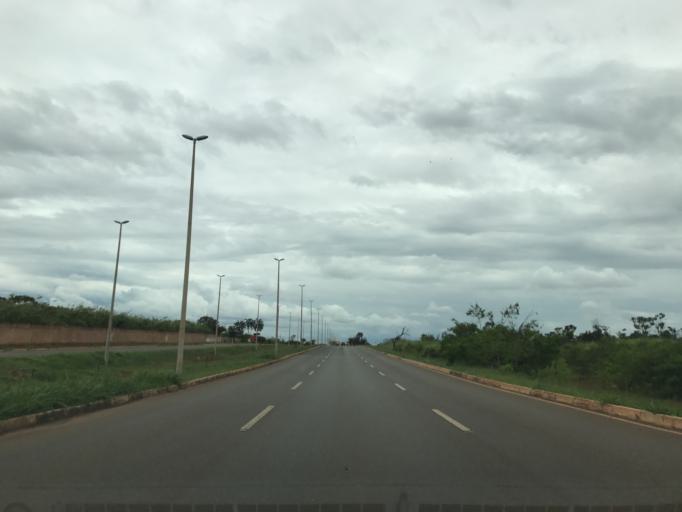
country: BR
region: Federal District
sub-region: Brasilia
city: Brasilia
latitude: -15.8007
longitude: -47.9915
